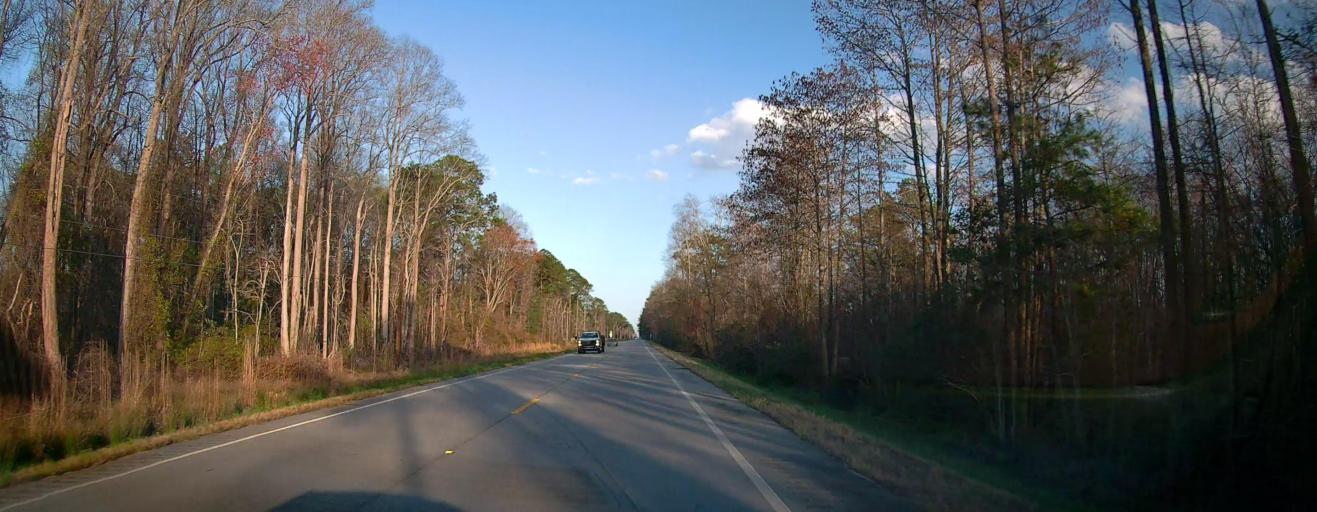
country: US
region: Georgia
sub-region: Bryan County
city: Pembroke
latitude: 32.1423
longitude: -81.7166
